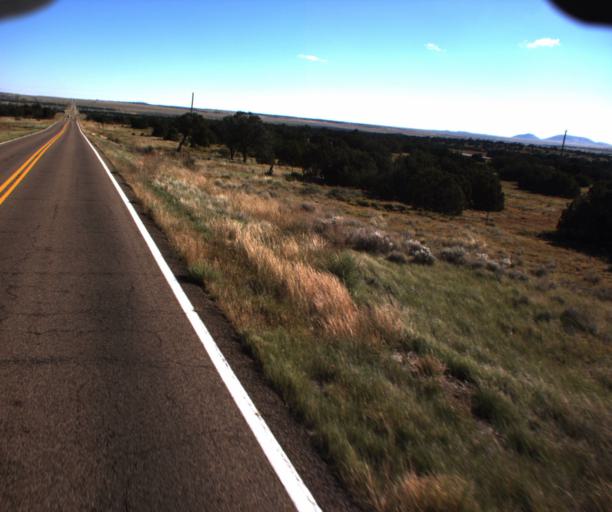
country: US
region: Arizona
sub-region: Navajo County
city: White Mountain Lake
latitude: 34.3314
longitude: -109.7450
